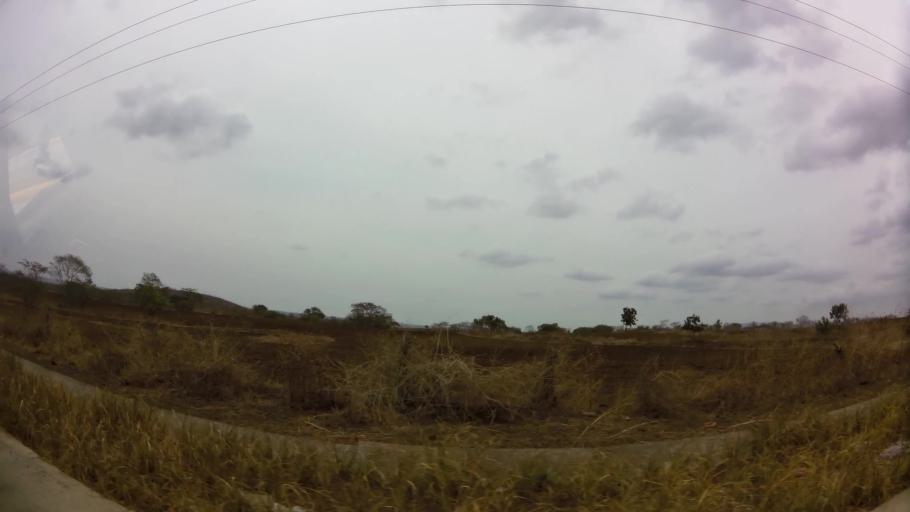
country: NI
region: Masaya
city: Ticuantepe
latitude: 12.0926
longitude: -86.1807
